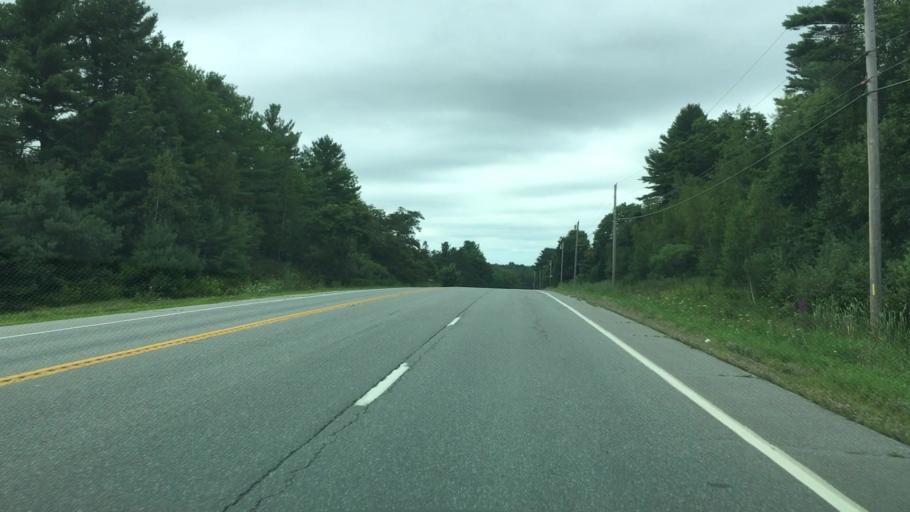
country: US
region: Maine
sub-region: Waldo County
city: Winterport
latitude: 44.6772
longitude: -68.8410
